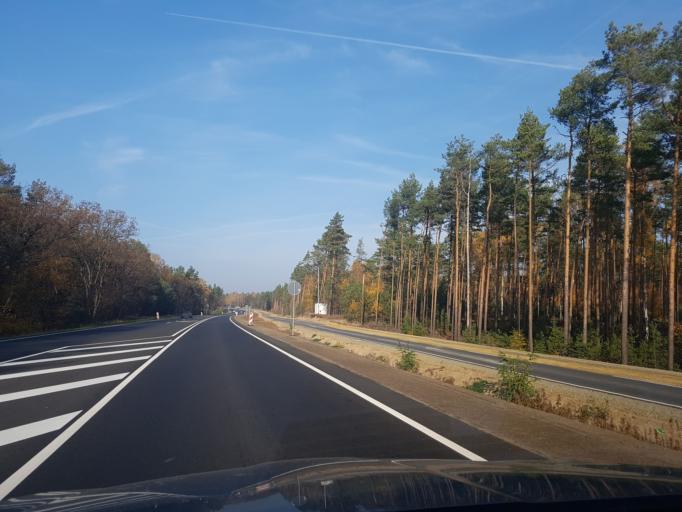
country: DE
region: Brandenburg
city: Elsterwerda
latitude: 51.4998
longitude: 13.4679
